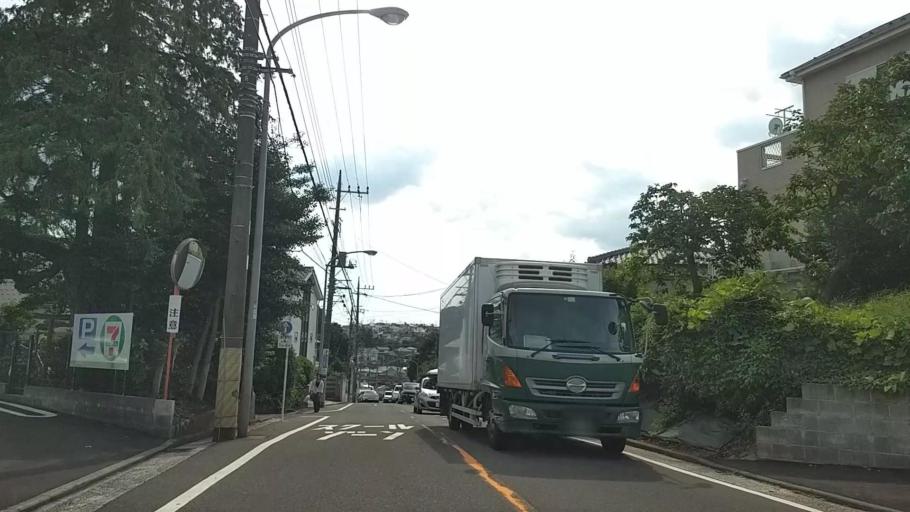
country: JP
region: Kanagawa
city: Yokohama
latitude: 35.4883
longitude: 139.5741
